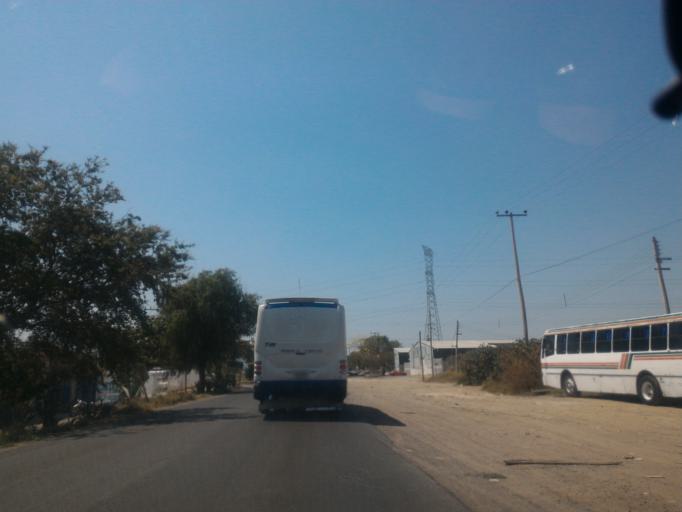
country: MX
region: Jalisco
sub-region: San Pedro Tlaquepaque
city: Paseo del Prado
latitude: 20.5643
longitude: -103.4126
